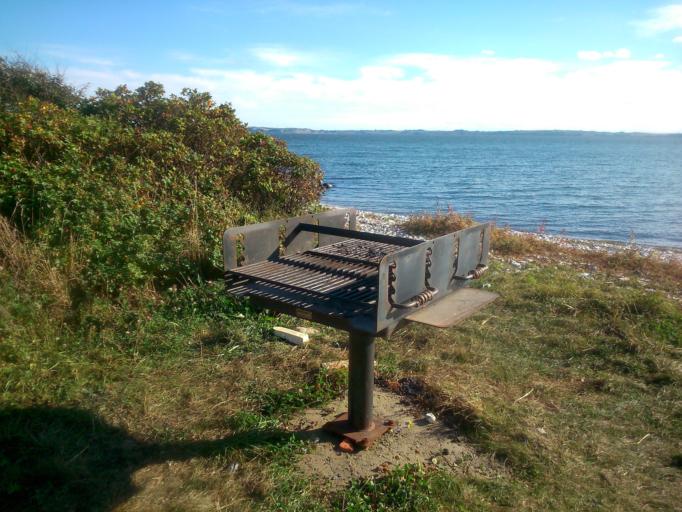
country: DK
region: North Denmark
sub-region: Thisted Kommune
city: Thisted
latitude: 56.9510
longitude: 8.6933
